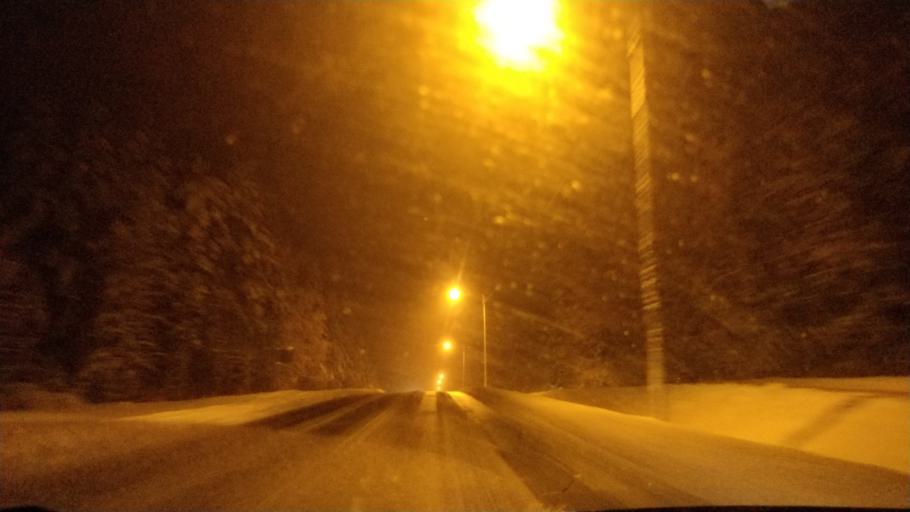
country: FI
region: Lapland
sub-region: Rovaniemi
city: Rovaniemi
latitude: 66.4262
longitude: 25.4238
